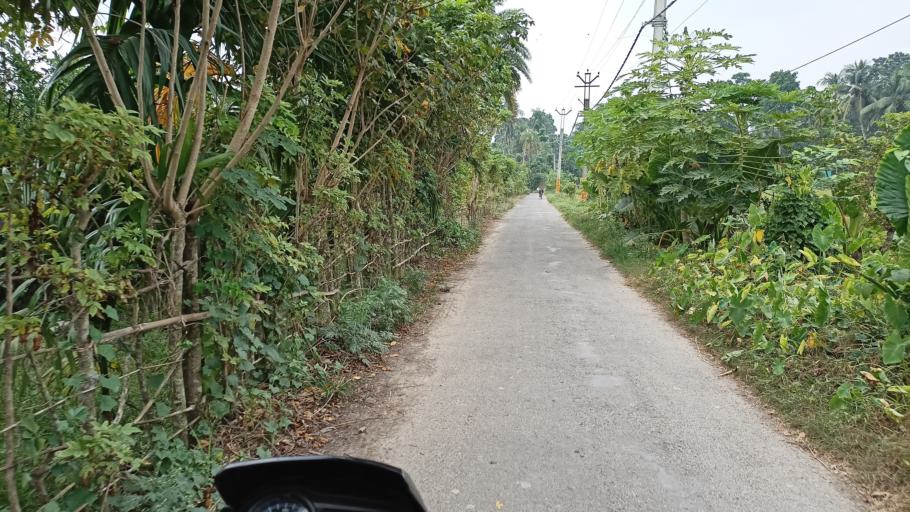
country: IN
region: West Bengal
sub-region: North 24 Parganas
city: Bangaon
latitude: 23.0636
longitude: 88.8194
